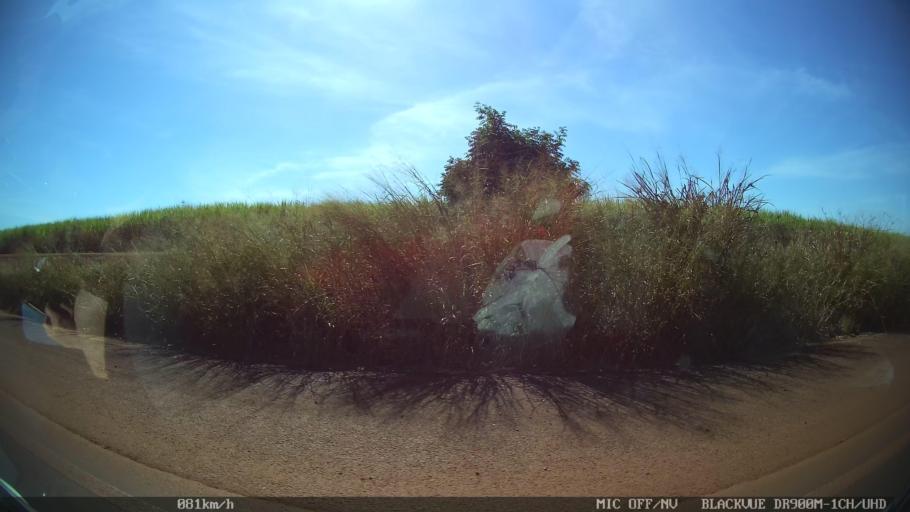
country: BR
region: Sao Paulo
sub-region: Barretos
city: Barretos
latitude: -20.4464
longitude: -48.4340
